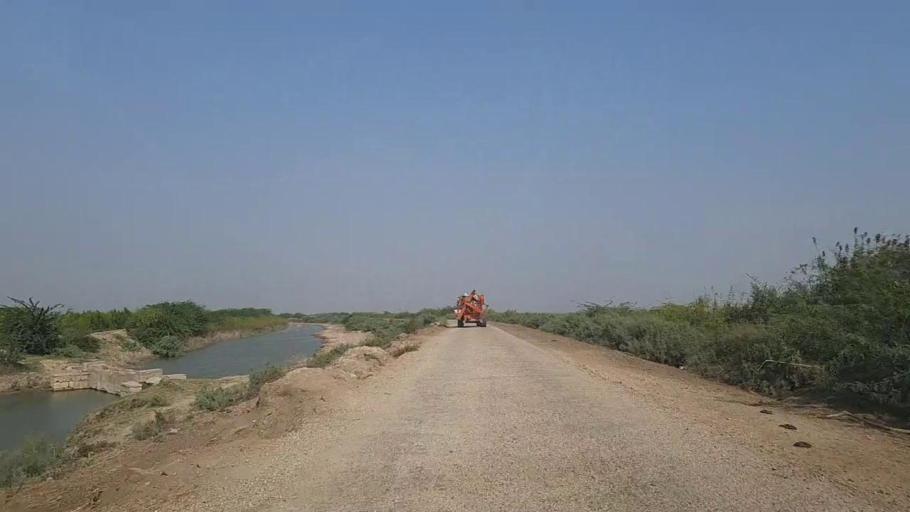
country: PK
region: Sindh
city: Keti Bandar
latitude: 24.2247
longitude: 67.6739
